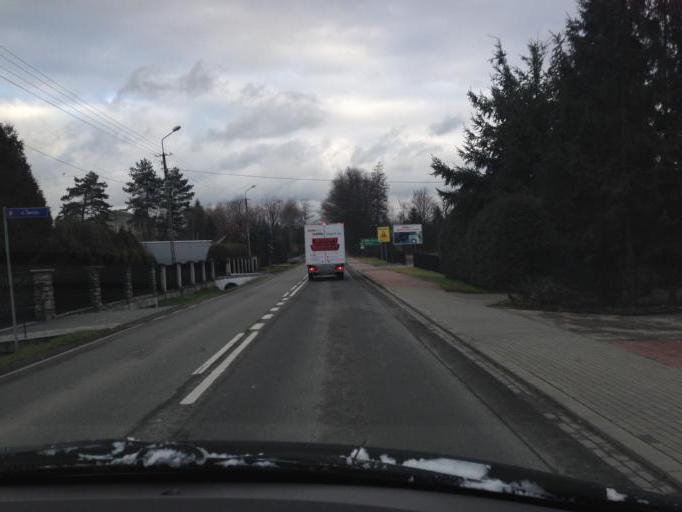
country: PL
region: Lesser Poland Voivodeship
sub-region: Powiat wielicki
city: Gdow
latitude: 49.9082
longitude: 20.1901
